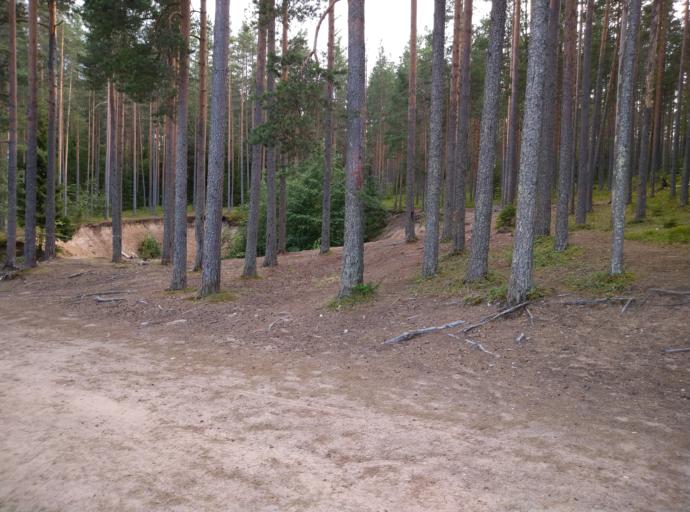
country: RU
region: Leningrad
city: Kuznechnoye
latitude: 61.0106
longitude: 29.6555
